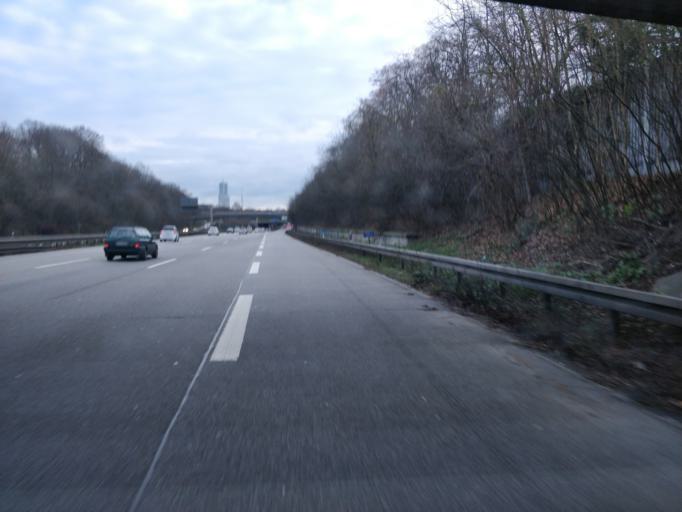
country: DE
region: North Rhine-Westphalia
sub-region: Regierungsbezirk Koln
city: Bilderstoeckchen
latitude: 50.9634
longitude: 6.9242
